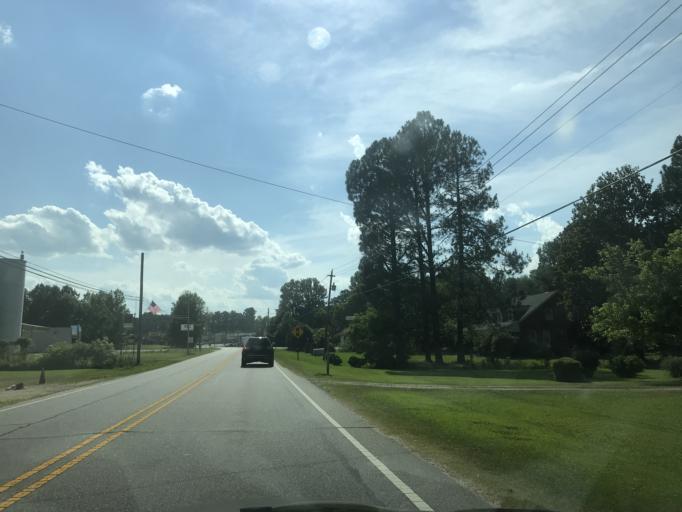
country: US
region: North Carolina
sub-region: Nash County
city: Spring Hope
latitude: 35.9517
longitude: -78.1011
